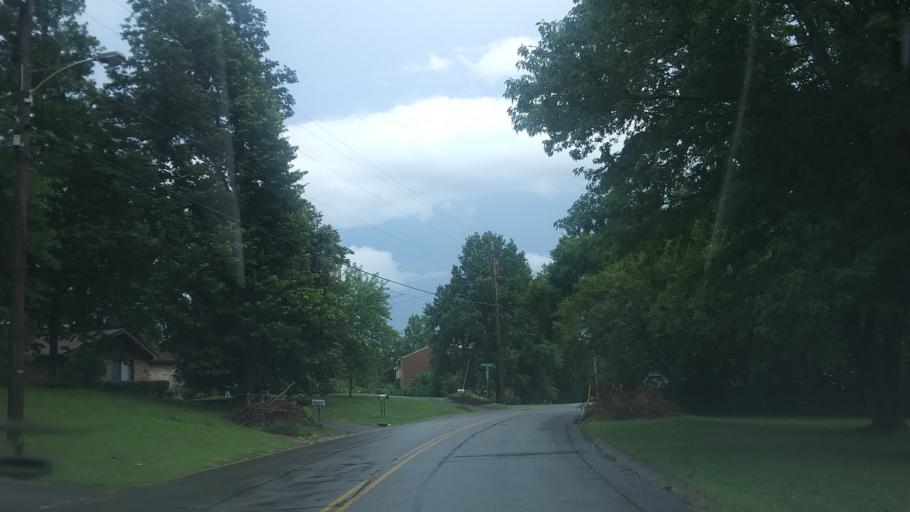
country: US
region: Tennessee
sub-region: Davidson County
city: Belle Meade
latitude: 36.1543
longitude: -86.8857
